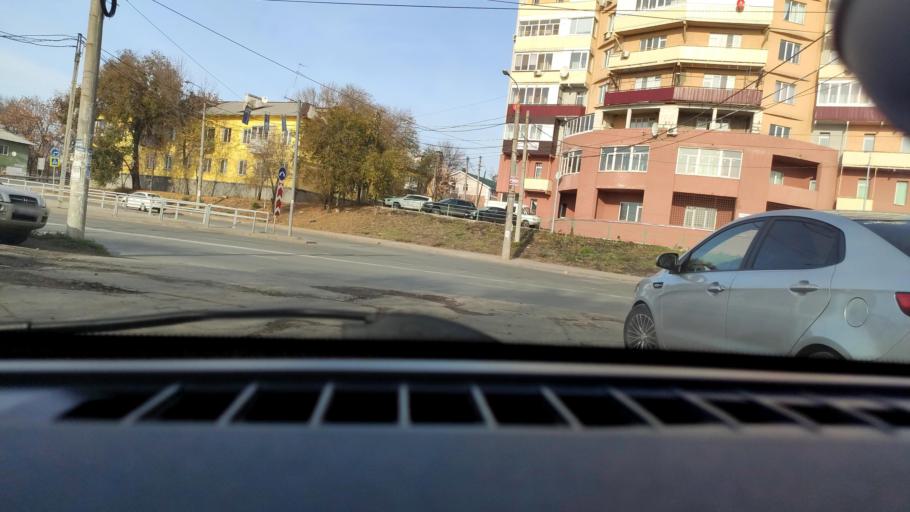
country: RU
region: Samara
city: Samara
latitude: 53.1794
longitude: 50.1934
